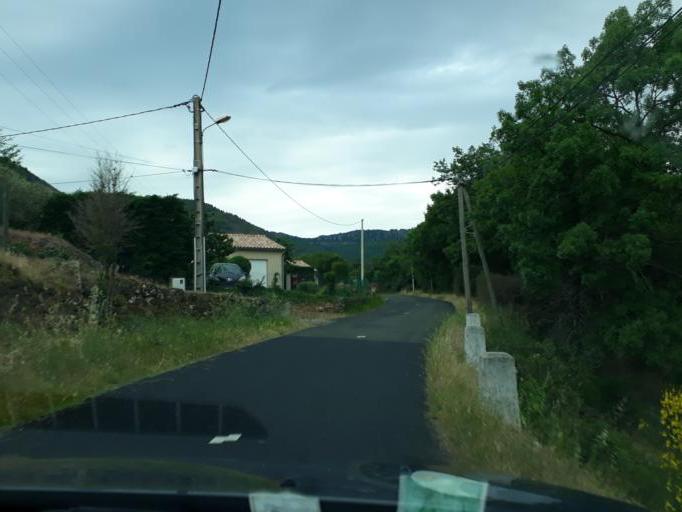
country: FR
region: Languedoc-Roussillon
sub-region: Departement de l'Herault
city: Lodeve
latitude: 43.7757
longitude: 3.2935
